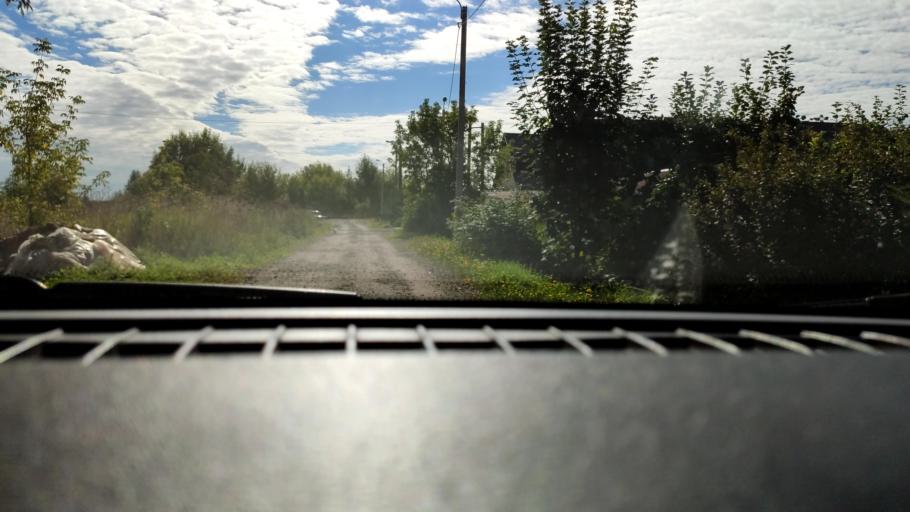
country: RU
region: Perm
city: Perm
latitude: 58.0159
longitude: 56.3373
